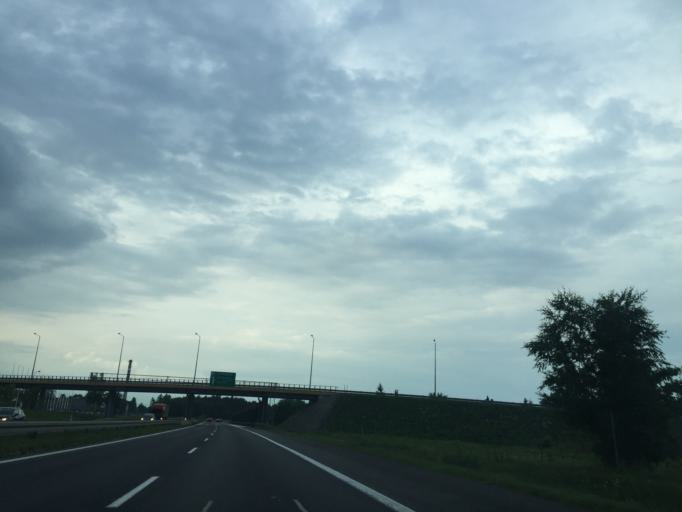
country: PL
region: Masovian Voivodeship
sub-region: Powiat ostrowski
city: Ostrow Mazowiecka
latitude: 52.8093
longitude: 21.8769
